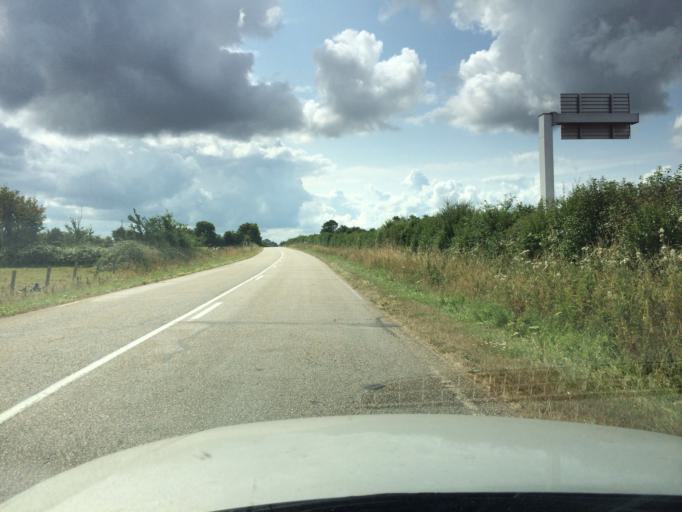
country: FR
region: Lower Normandy
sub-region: Departement de la Manche
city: Sainte-Mere-Eglise
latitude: 49.4238
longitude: -1.3289
